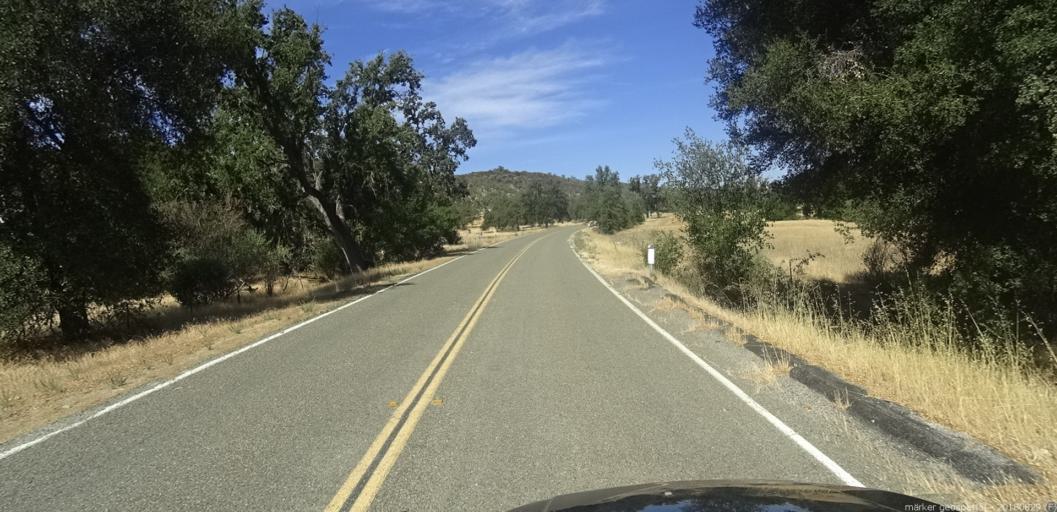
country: US
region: California
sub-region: San Luis Obispo County
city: Lake Nacimiento
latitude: 35.8043
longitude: -120.9903
